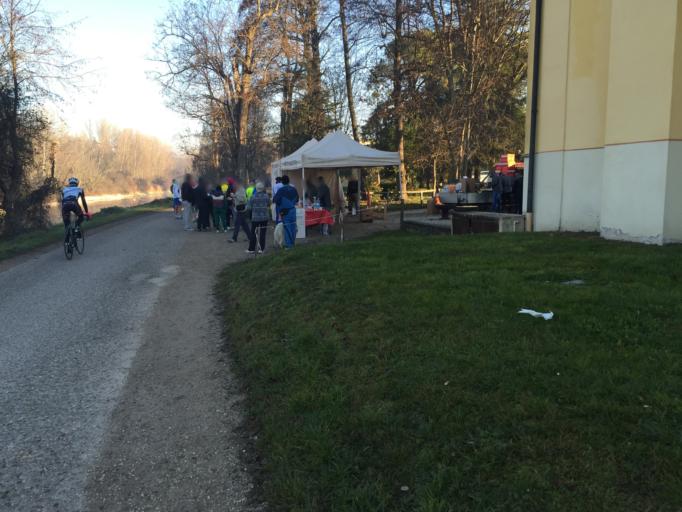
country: IT
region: Lombardy
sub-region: Provincia di Mantova
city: Monzambano
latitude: 45.3849
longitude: 10.6965
